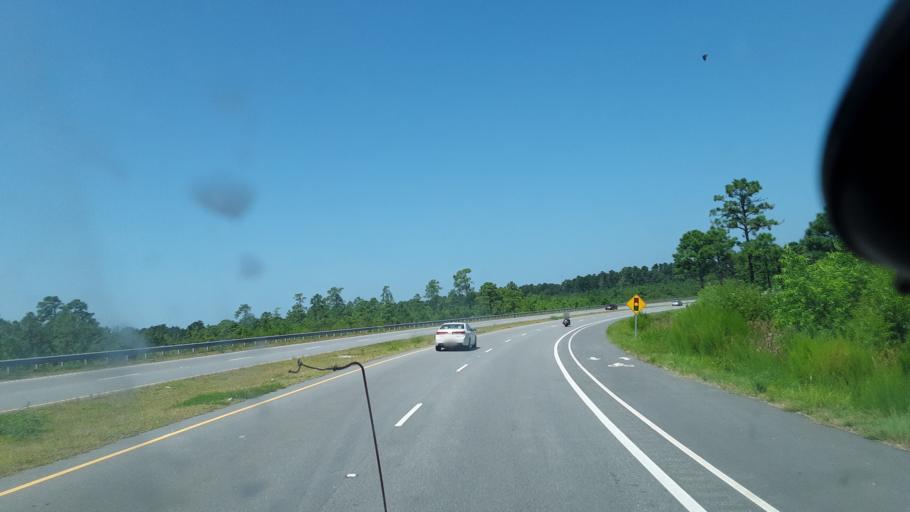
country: US
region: South Carolina
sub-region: Horry County
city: Forestbrook
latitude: 33.8181
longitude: -78.9127
